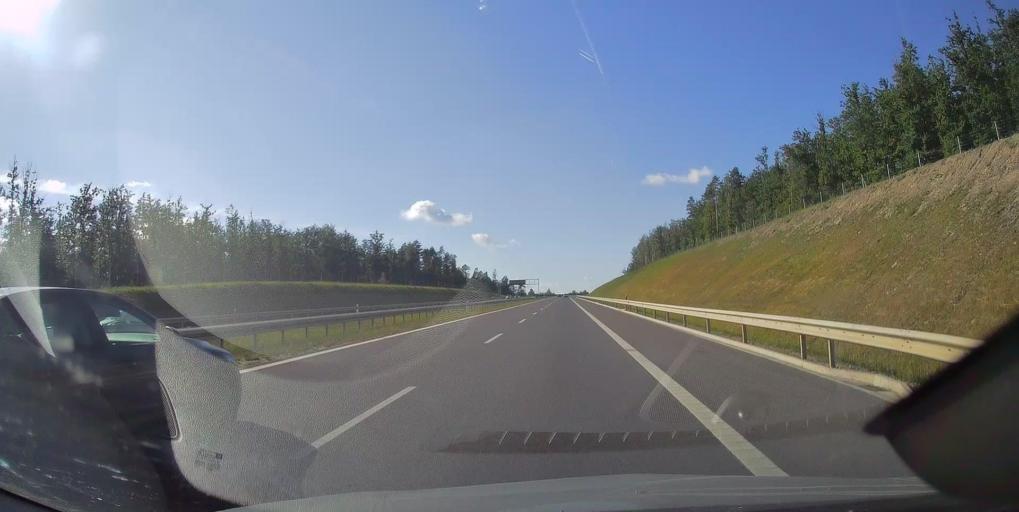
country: PL
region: Swietokrzyskie
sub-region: Powiat skarzyski
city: Skarzysko-Kamienna
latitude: 51.1285
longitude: 20.8396
